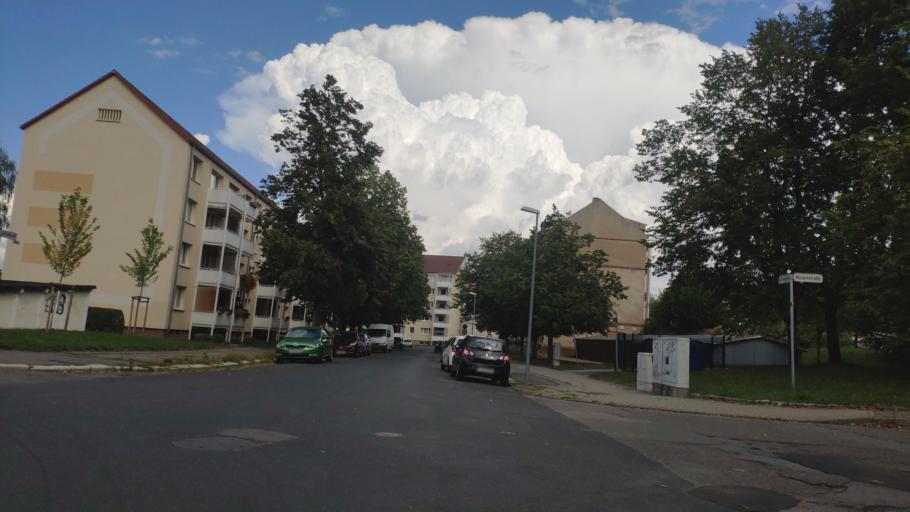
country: DE
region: Saxony
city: Chemnitz
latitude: 50.8213
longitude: 12.9042
